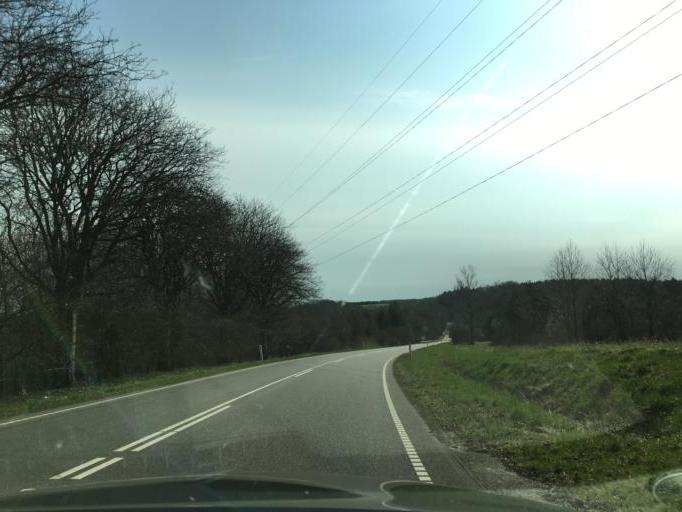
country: DK
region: South Denmark
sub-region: Kolding Kommune
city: Lunderskov
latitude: 55.5079
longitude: 9.3531
